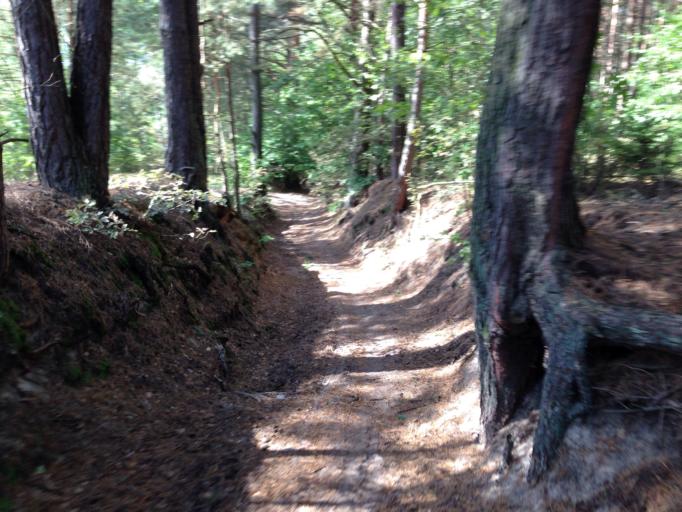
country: PL
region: Warmian-Masurian Voivodeship
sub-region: Powiat dzialdowski
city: Lidzbark
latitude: 53.2177
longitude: 19.7502
